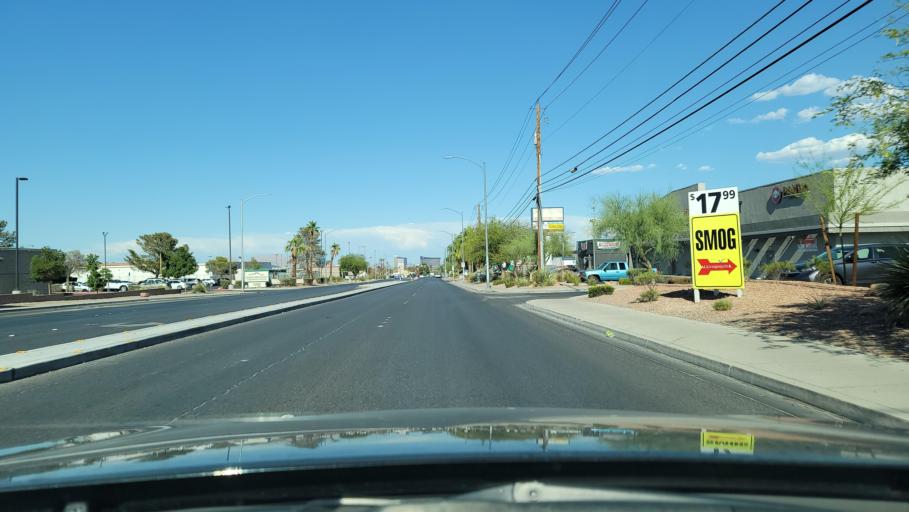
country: US
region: Nevada
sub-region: Clark County
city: Spring Valley
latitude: 36.1256
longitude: -115.2471
